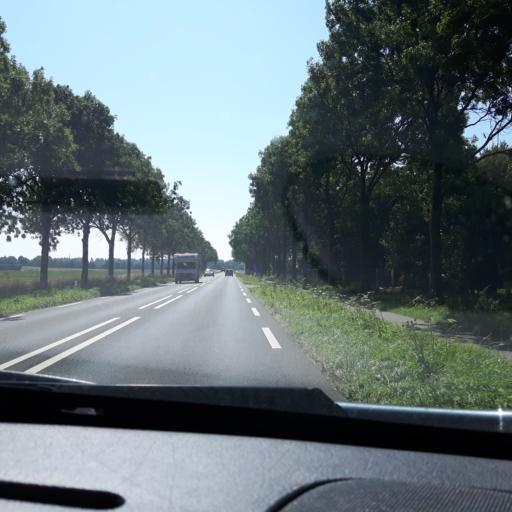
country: NL
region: Zeeland
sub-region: Gemeente Goes
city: Goes
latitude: 51.4705
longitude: 3.9034
